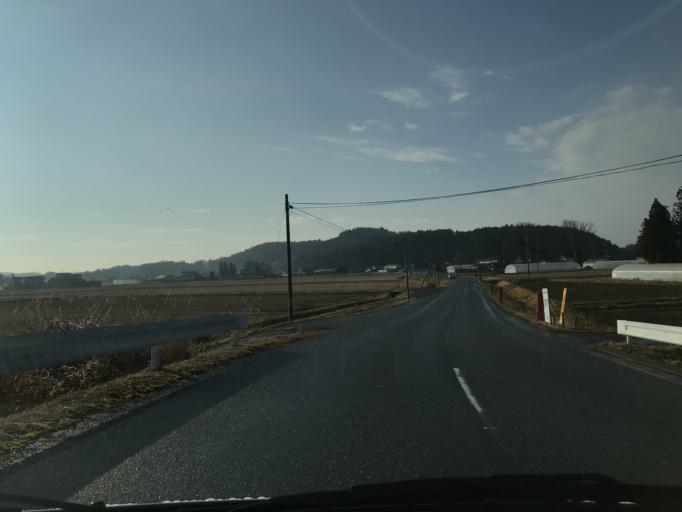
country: JP
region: Iwate
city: Ichinoseki
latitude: 38.7805
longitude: 141.1770
